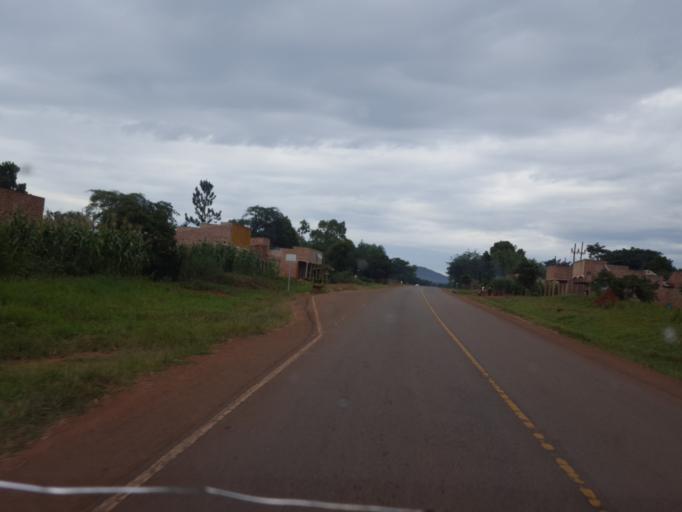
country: UG
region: Central Region
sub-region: Kiboga District
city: Kiboga
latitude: 1.0109
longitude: 31.6940
